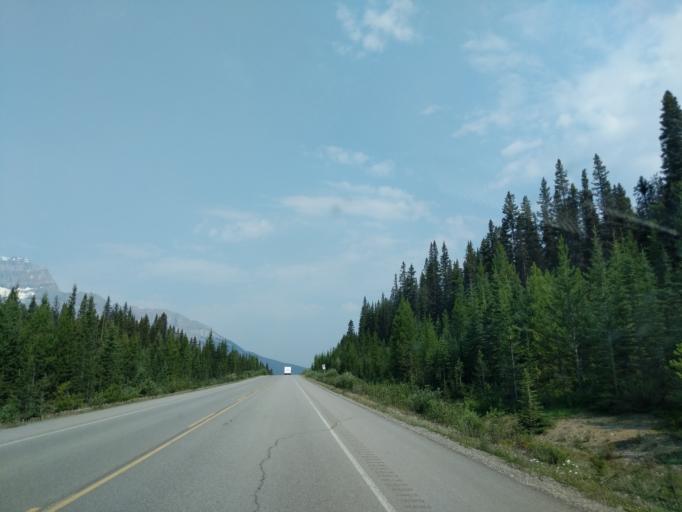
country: CA
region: Alberta
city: Lake Louise
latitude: 51.8691
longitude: -116.6695
